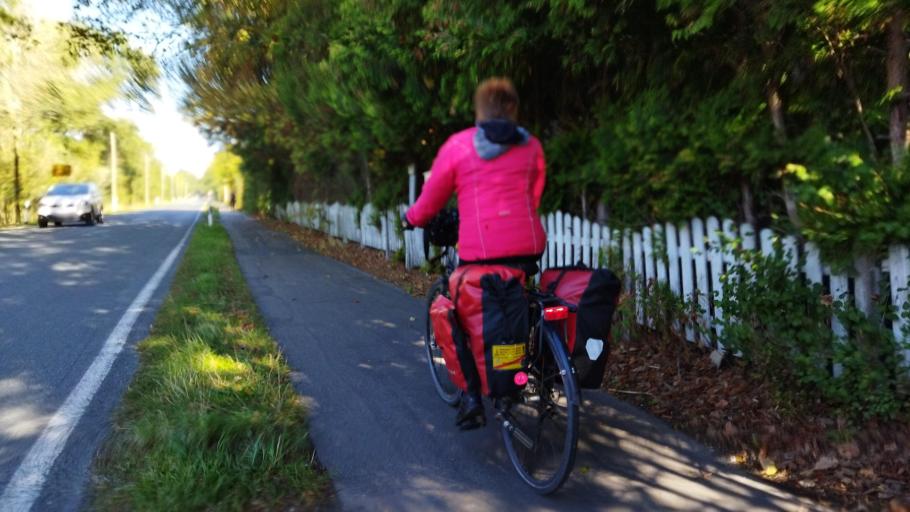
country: DE
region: Lower Saxony
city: Ohne
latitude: 52.2583
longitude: 7.3152
